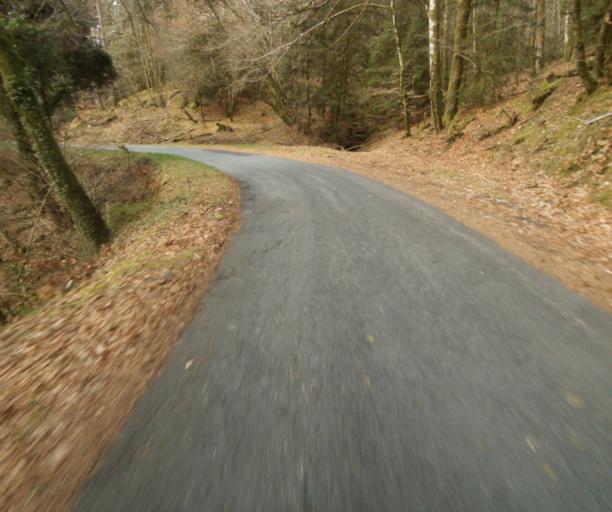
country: FR
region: Limousin
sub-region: Departement de la Correze
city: Correze
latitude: 45.3877
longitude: 1.8892
